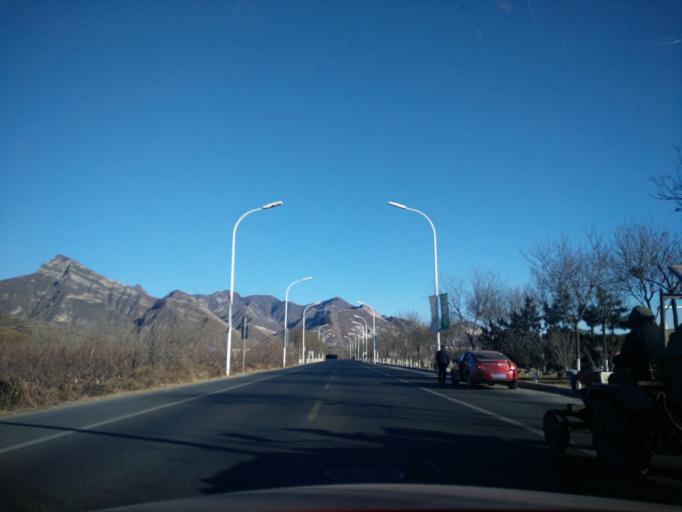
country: CN
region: Beijing
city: Junzhuang
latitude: 39.9870
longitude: 116.0808
